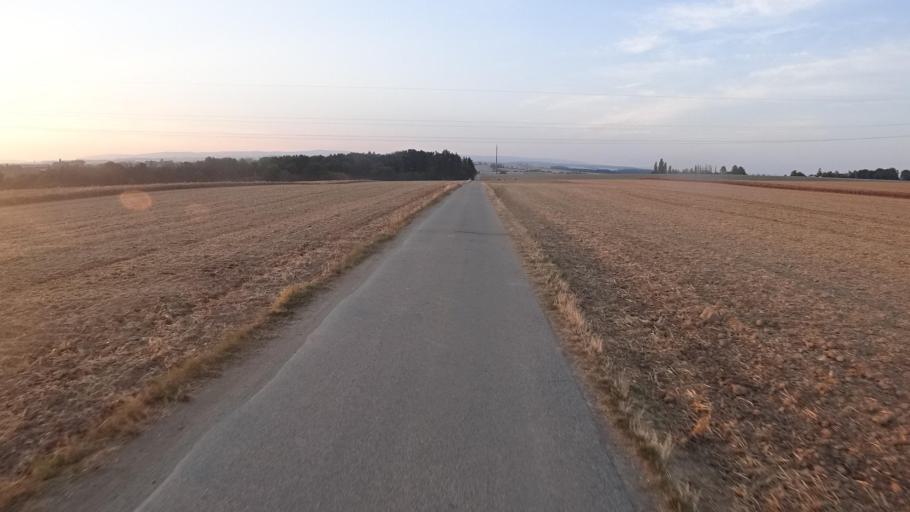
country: DE
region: Rheinland-Pfalz
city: Keidelheim
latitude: 49.9865
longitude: 7.5008
